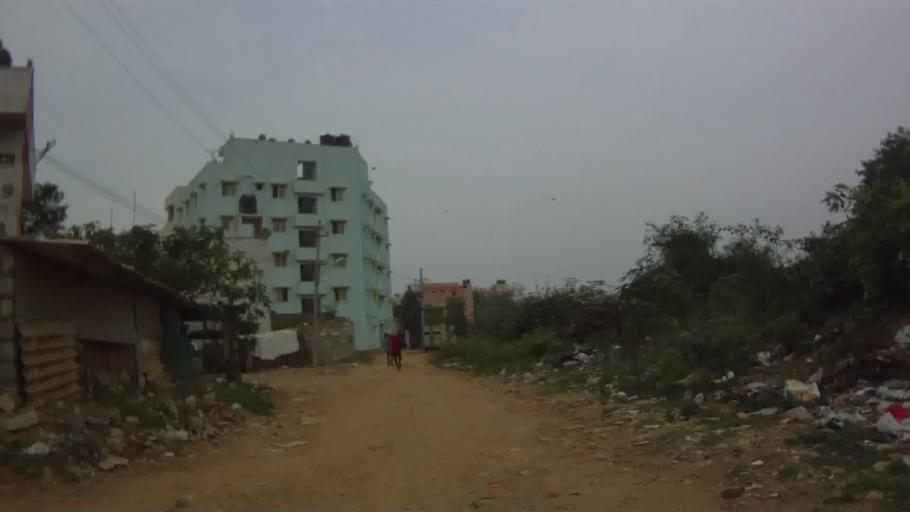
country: IN
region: Karnataka
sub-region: Bangalore Urban
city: Bangalore
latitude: 12.9706
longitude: 77.7019
